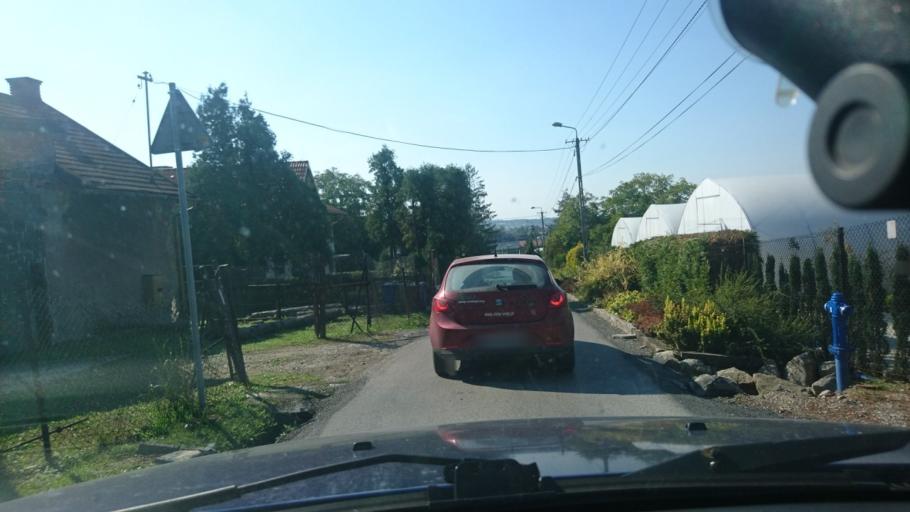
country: PL
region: Silesian Voivodeship
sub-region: Bielsko-Biala
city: Bielsko-Biala
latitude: 49.8451
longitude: 19.0729
